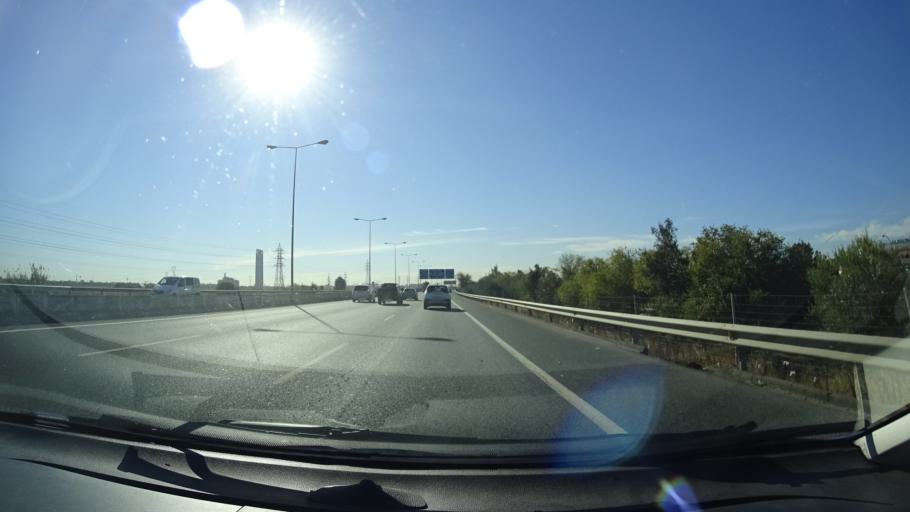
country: ES
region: Andalusia
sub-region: Provincia de Sevilla
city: Camas
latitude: 37.4031
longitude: -6.0290
